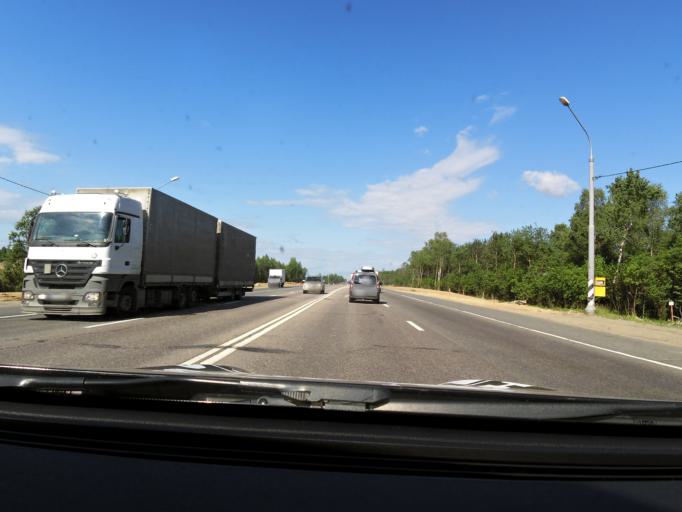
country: RU
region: Tverskaya
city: Emmaus
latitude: 56.7831
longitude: 36.0131
